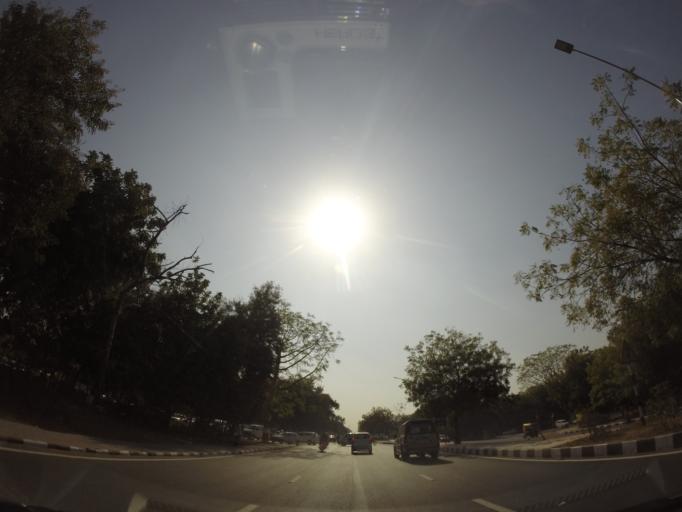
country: IN
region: Gujarat
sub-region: Gandhinagar
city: Ghandinagar
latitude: 23.2209
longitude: 72.6439
